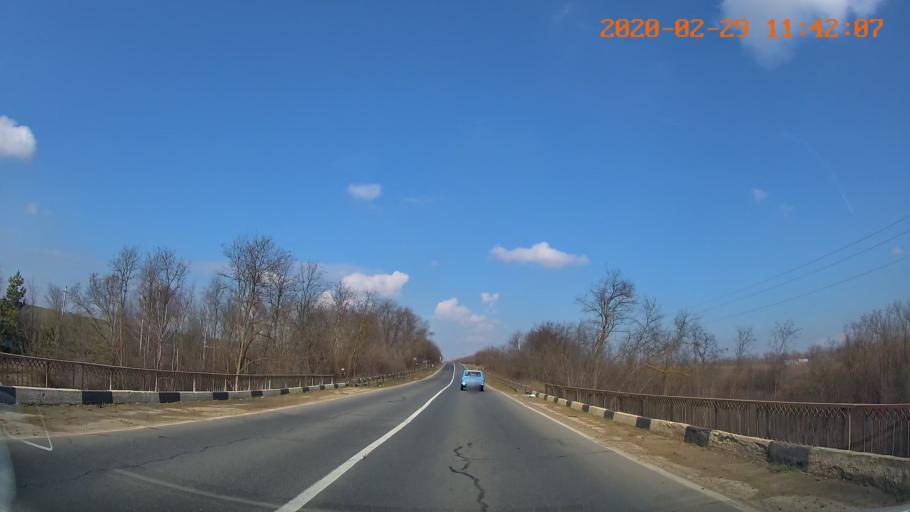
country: MD
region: Rezina
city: Saharna
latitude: 47.6799
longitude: 29.0142
